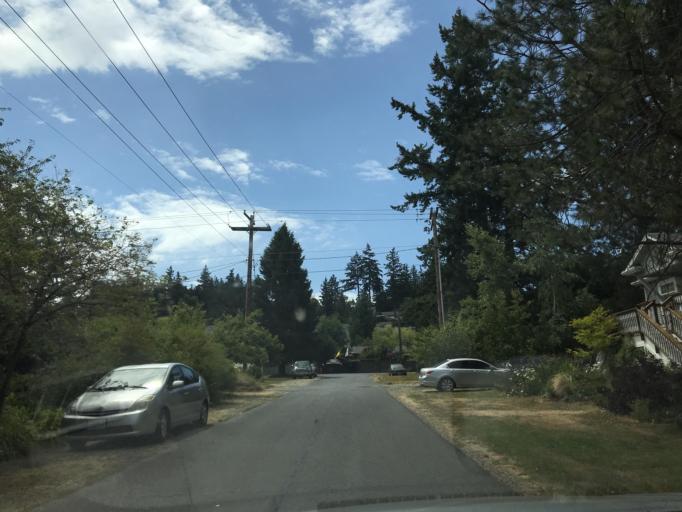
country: US
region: Washington
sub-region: Whatcom County
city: Bellingham
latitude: 48.7167
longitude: -122.5093
